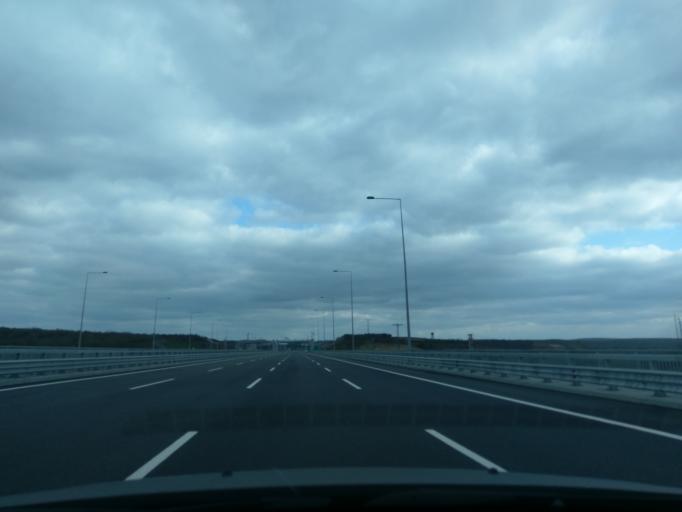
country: TR
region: Istanbul
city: Kemerburgaz
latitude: 41.2375
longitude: 28.8120
